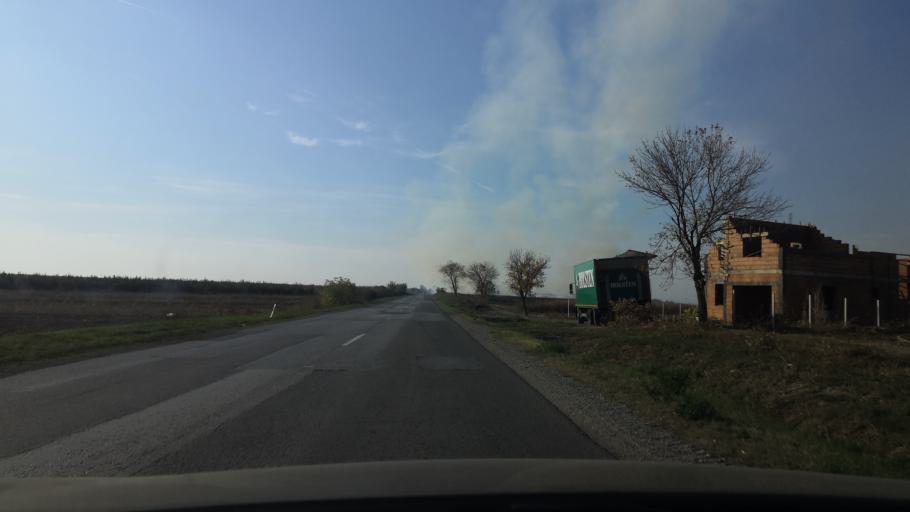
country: RS
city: Putinci
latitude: 44.9963
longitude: 19.9570
